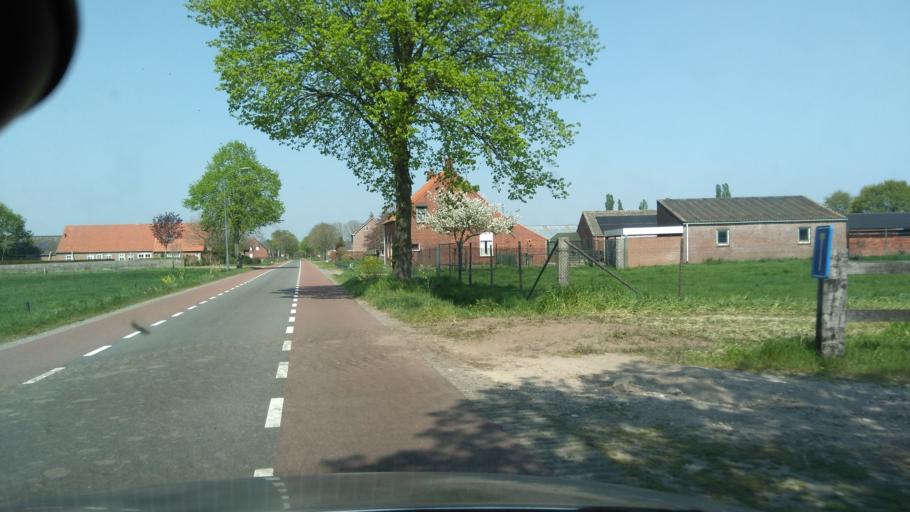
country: BE
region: Flanders
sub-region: Provincie Antwerpen
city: Baarle-Hertog
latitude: 51.4655
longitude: 4.8574
